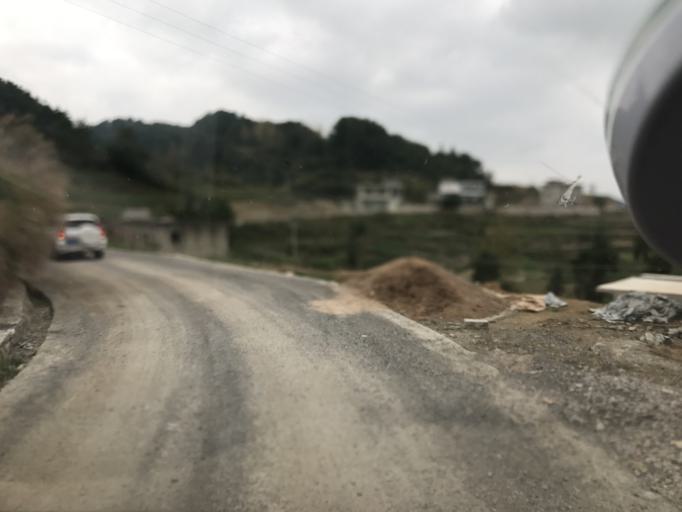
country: CN
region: Guizhou Sheng
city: Donghua
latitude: 28.0554
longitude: 108.1079
